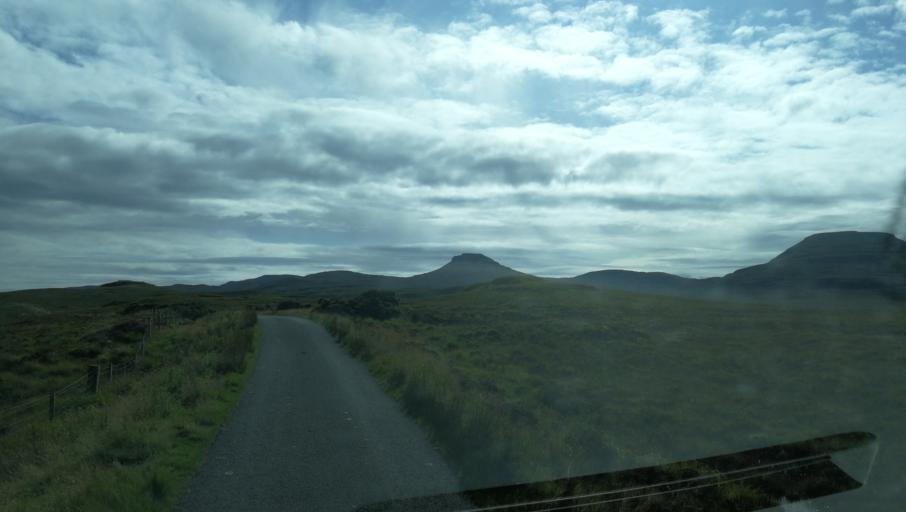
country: GB
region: Scotland
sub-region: Highland
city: Isle of Skye
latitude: 57.4197
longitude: -6.5646
